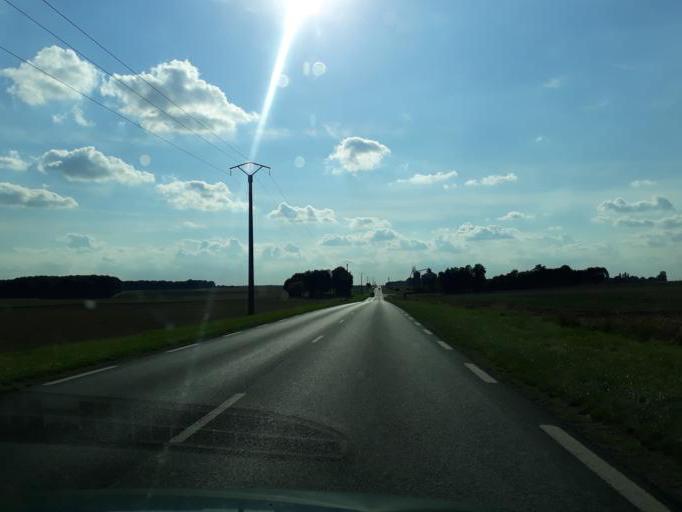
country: FR
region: Centre
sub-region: Departement du Loir-et-Cher
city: Oucques
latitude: 47.9041
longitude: 1.3609
